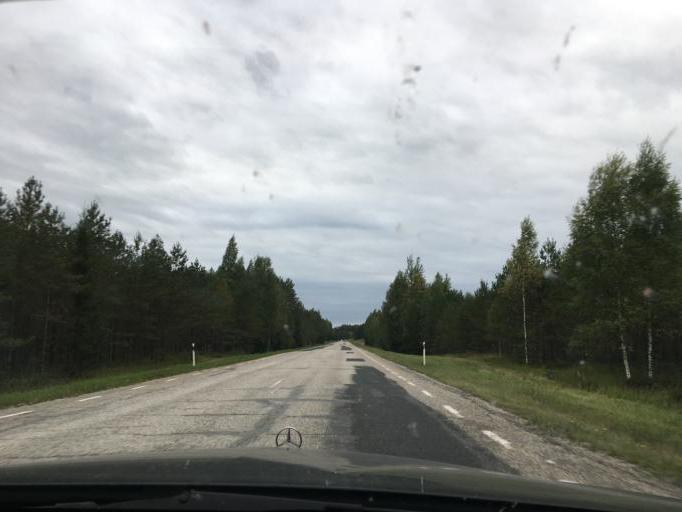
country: LV
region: Aluksnes Rajons
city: Aluksne
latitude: 57.5991
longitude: 27.1231
